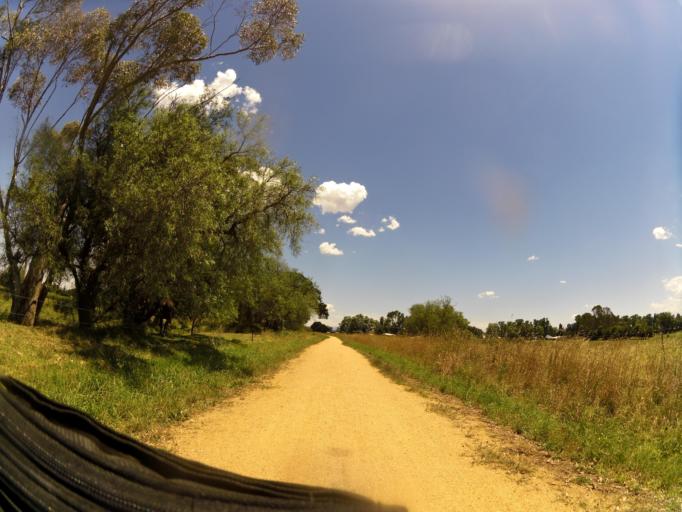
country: AU
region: Victoria
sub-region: Wellington
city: Heyfield
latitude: -37.9647
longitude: 146.8947
